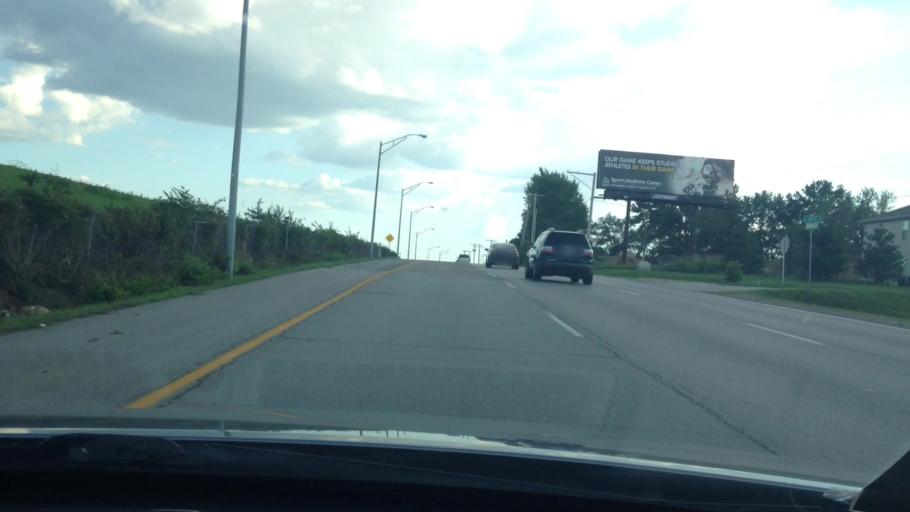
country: US
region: Missouri
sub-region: Clay County
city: Claycomo
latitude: 39.1793
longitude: -94.4936
